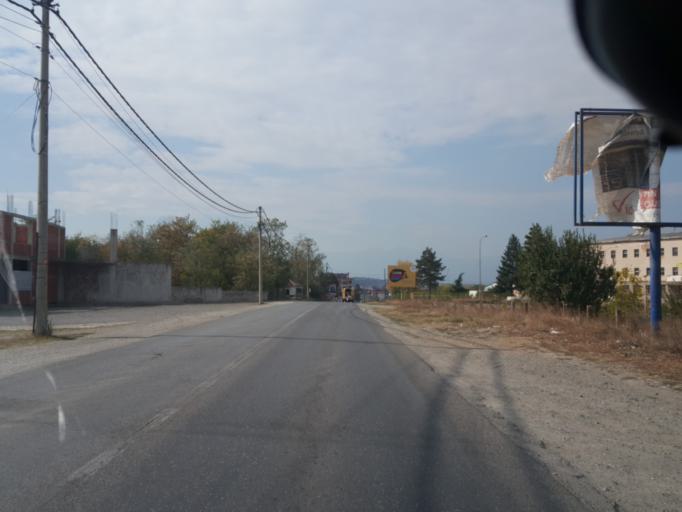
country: XK
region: Gjakova
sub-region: Komuna e Gjakoves
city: Gjakove
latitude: 42.3718
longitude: 20.4511
